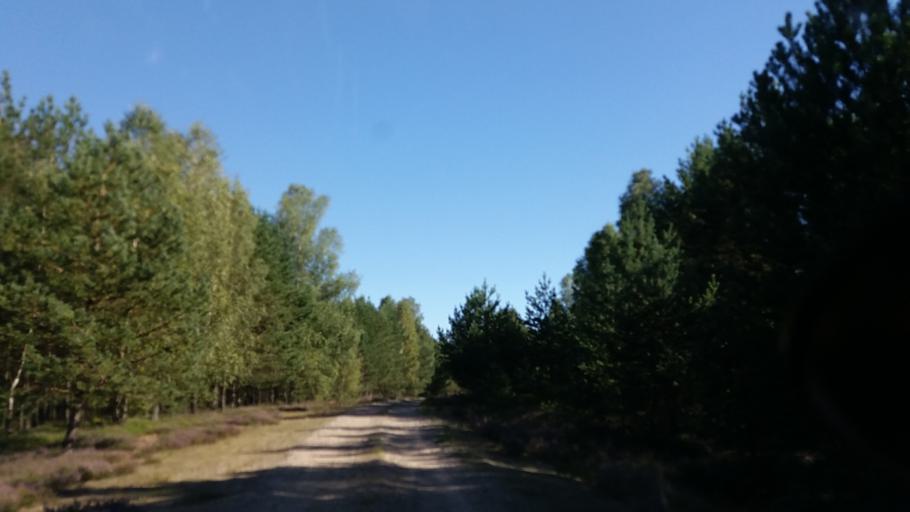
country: PL
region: West Pomeranian Voivodeship
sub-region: Powiat szczecinecki
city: Borne Sulinowo
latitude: 53.5666
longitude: 16.4983
